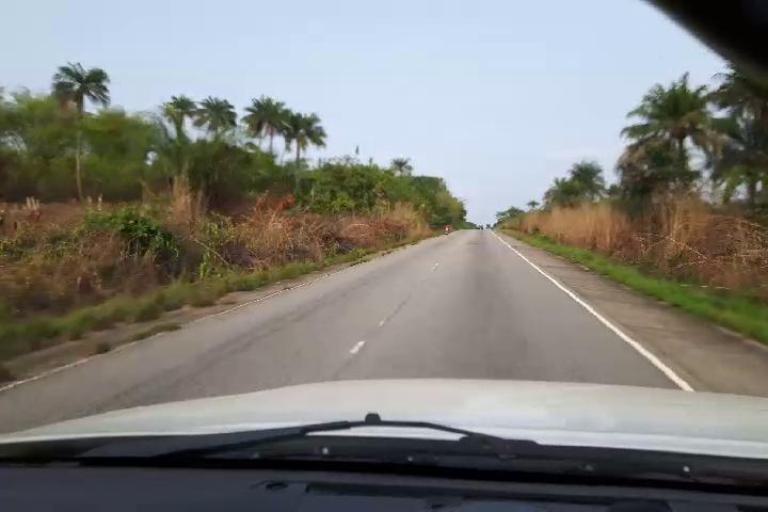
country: SL
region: Southern Province
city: Baoma
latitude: 7.9243
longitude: -11.5393
